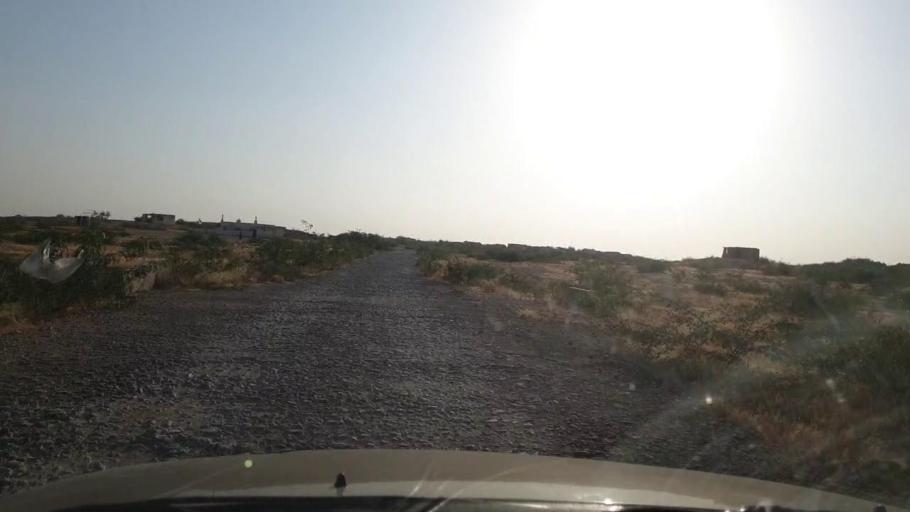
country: PK
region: Sindh
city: Kotri
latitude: 25.2101
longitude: 68.2151
